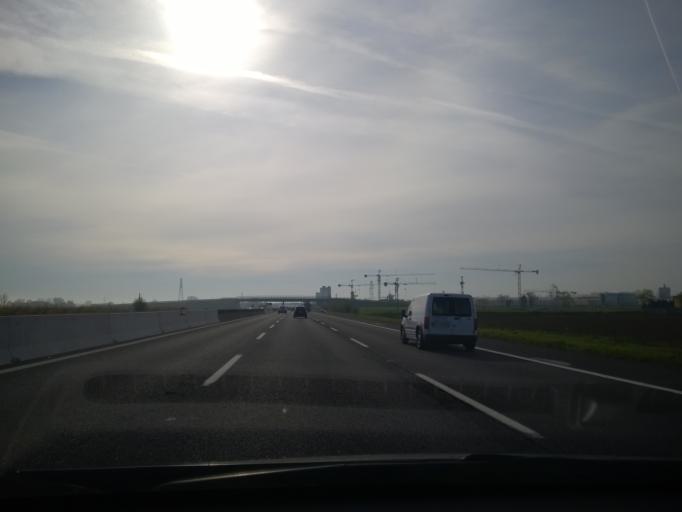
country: IT
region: Emilia-Romagna
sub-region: Provincia di Bologna
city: Imola
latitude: 44.3892
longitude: 11.7181
